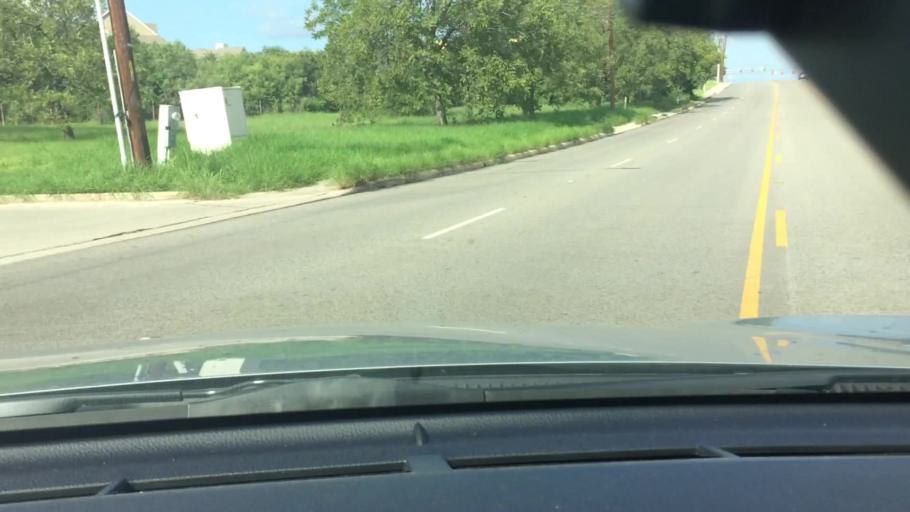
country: US
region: Texas
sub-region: Bexar County
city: Shavano Park
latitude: 29.5623
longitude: -98.5602
